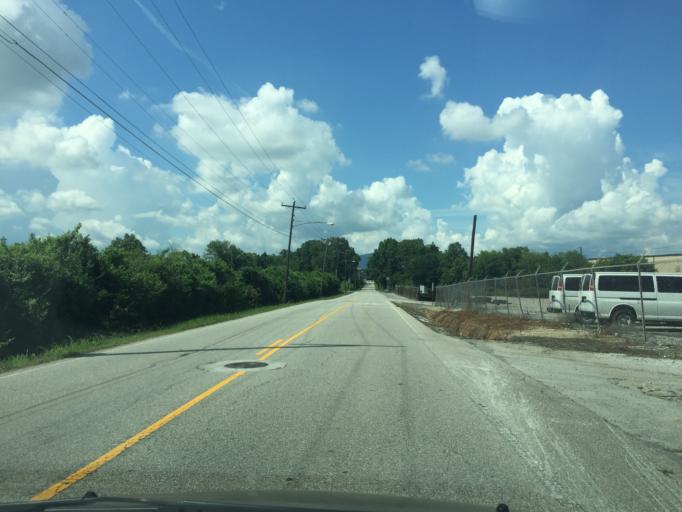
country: US
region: Tennessee
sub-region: Hamilton County
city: East Chattanooga
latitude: 35.0643
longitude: -85.2690
